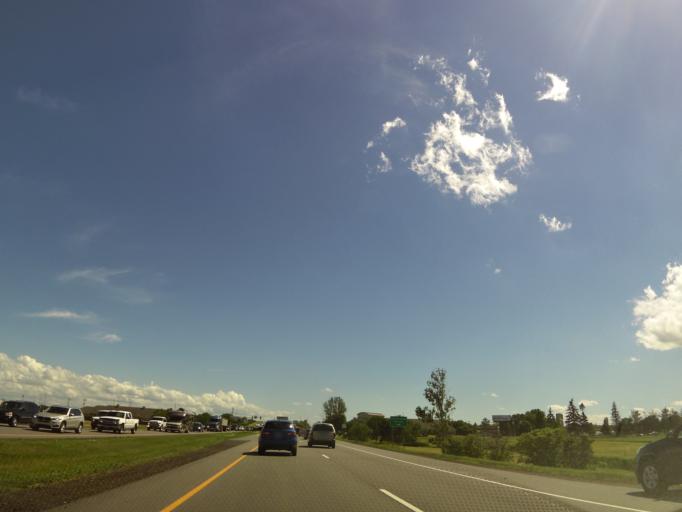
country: US
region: Minnesota
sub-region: Stearns County
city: Waite Park
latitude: 45.5683
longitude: -94.2061
